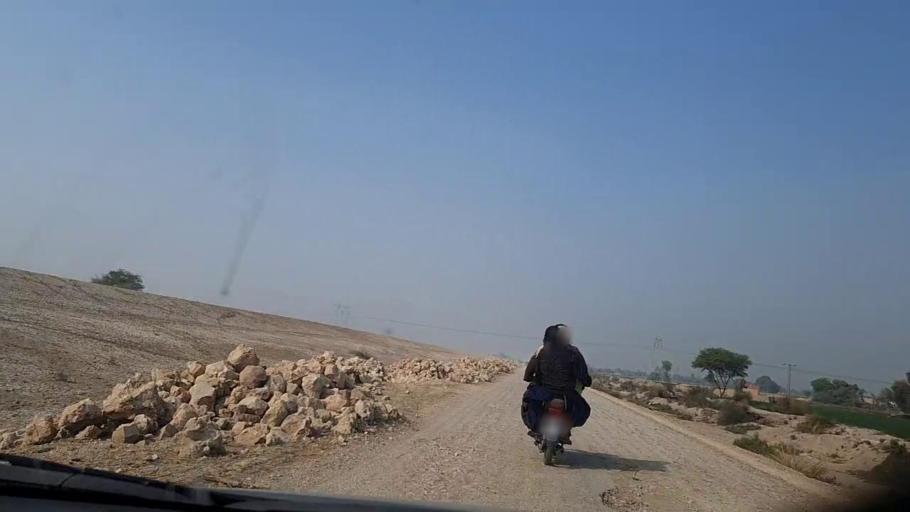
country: PK
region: Sindh
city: Moro
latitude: 26.7074
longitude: 67.9256
